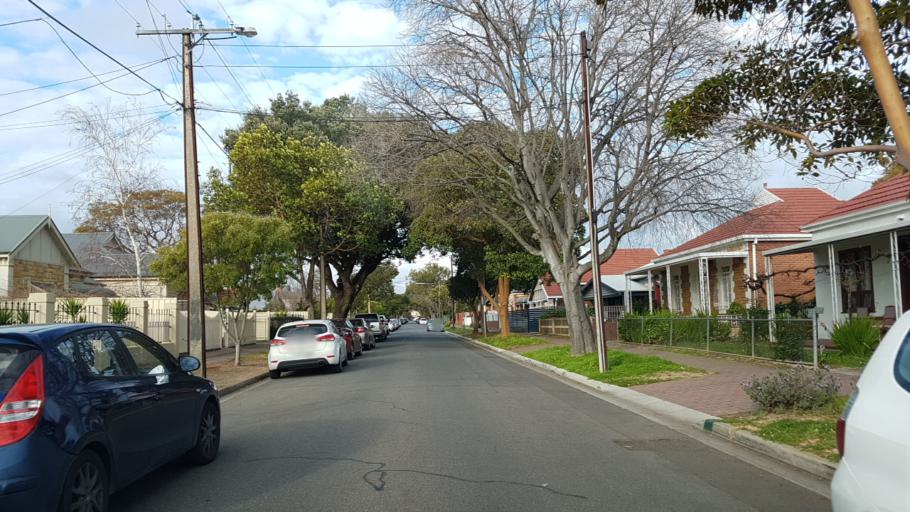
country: AU
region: South Australia
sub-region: Prospect
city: Prospect
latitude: -34.8880
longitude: 138.5979
